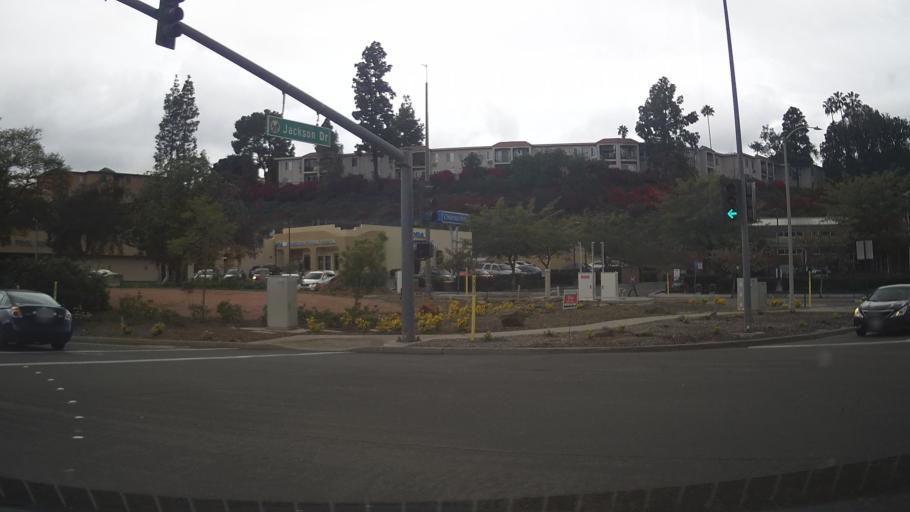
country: US
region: California
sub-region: San Diego County
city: La Mesa
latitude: 32.7773
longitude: -117.0181
